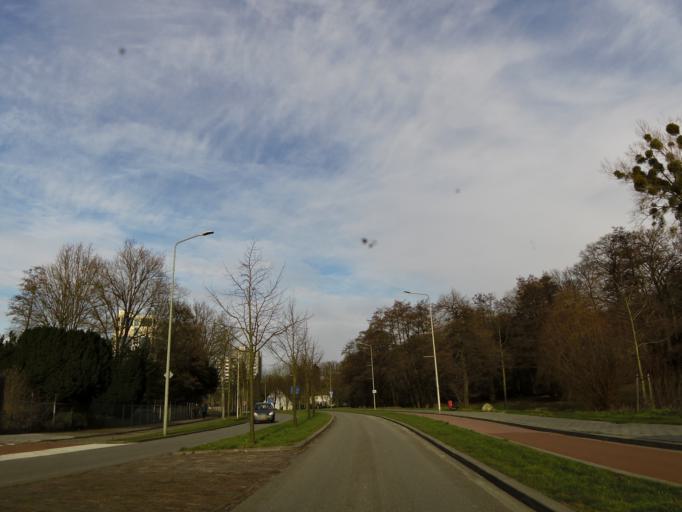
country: NL
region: Limburg
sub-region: Gemeente Heerlen
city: Heerlen
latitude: 50.8853
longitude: 5.9863
